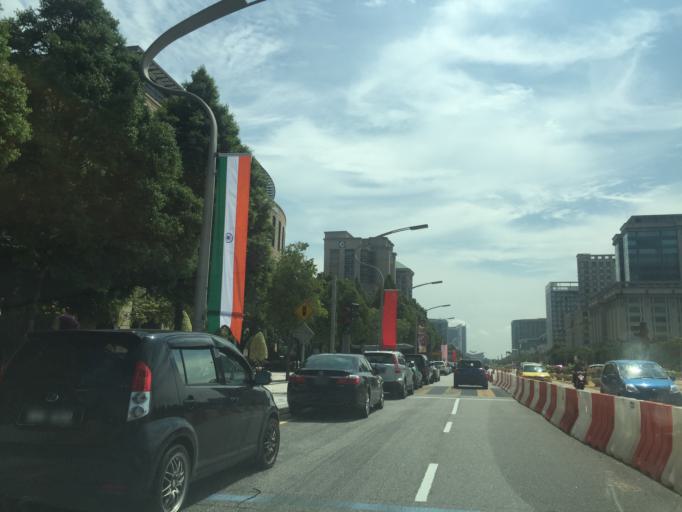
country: MY
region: Putrajaya
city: Putrajaya
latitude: 2.9238
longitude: 101.6873
